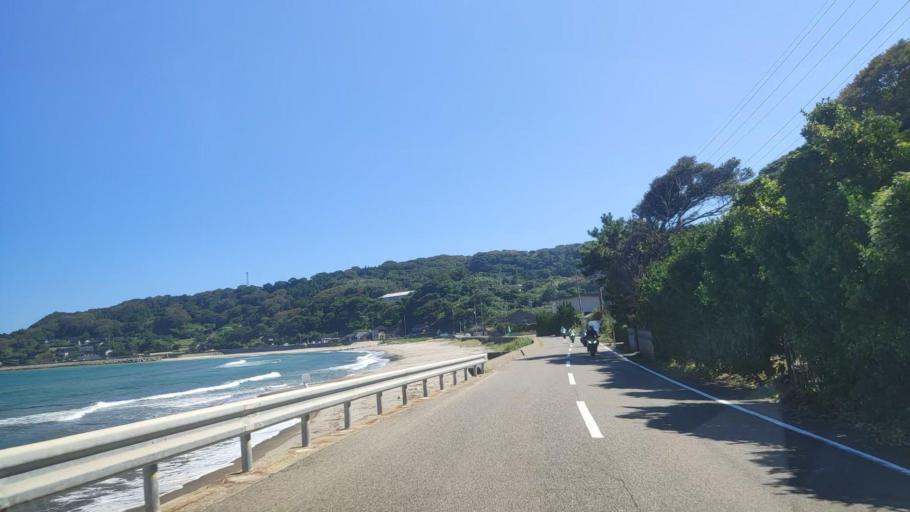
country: JP
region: Ishikawa
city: Nanao
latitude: 37.5284
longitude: 137.2787
